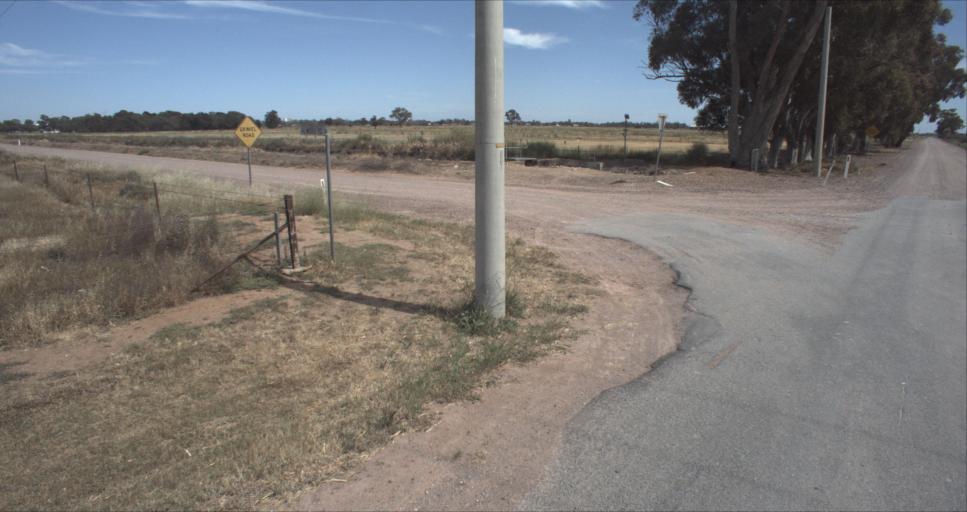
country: AU
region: New South Wales
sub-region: Leeton
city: Leeton
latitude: -34.5538
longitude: 146.4385
